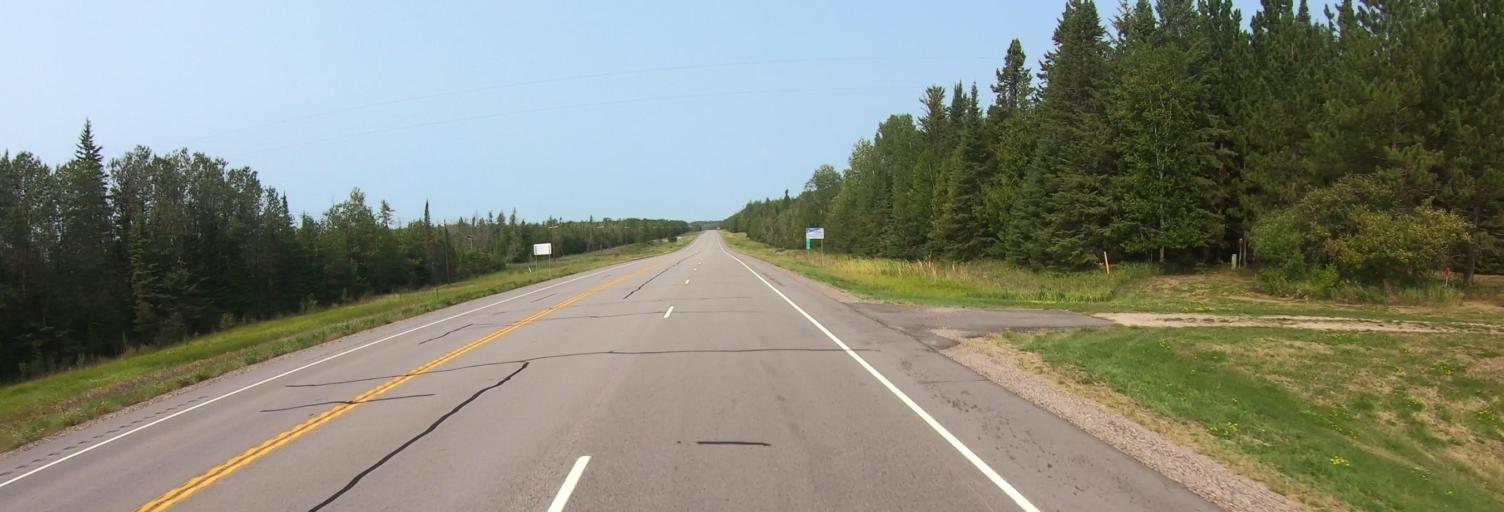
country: CA
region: Ontario
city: Fort Frances
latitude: 48.4023
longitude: -93.0233
